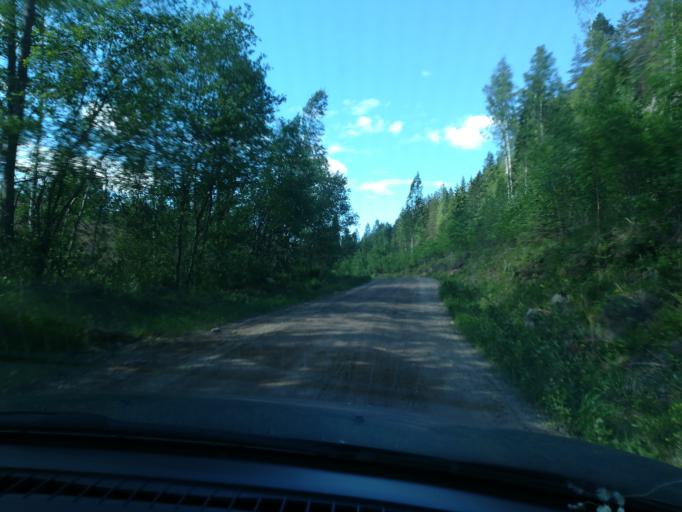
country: FI
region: Southern Savonia
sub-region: Mikkeli
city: Puumala
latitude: 61.6494
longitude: 28.1878
